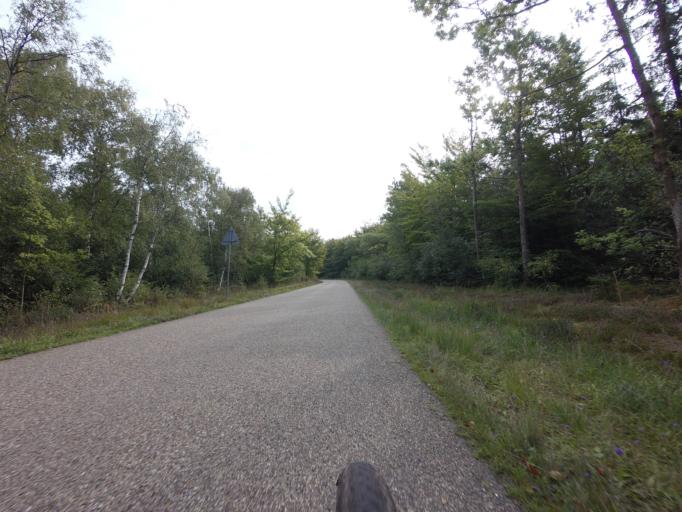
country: DK
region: North Denmark
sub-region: Hjorring Kommune
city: Hirtshals
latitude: 57.5791
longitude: 10.0722
